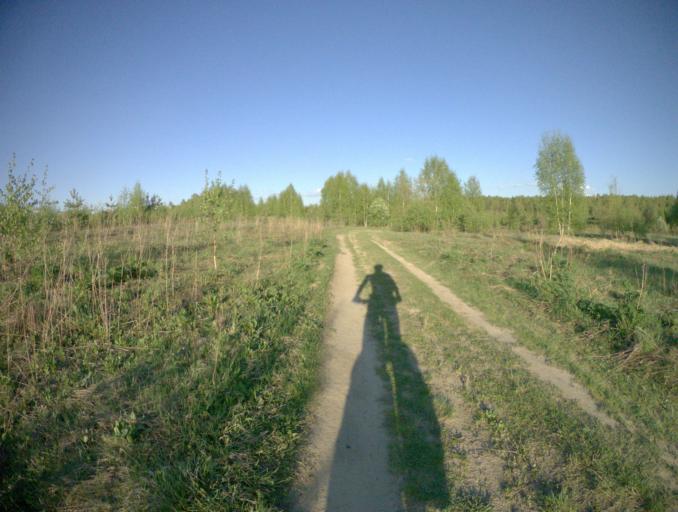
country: RU
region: Vladimir
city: Raduzhnyy
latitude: 55.9946
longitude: 40.2355
